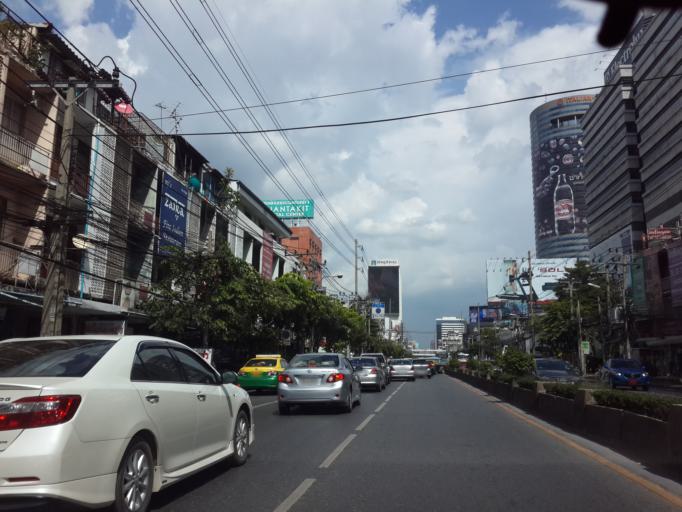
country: TH
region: Bangkok
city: Watthana
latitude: 13.7480
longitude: 100.5704
